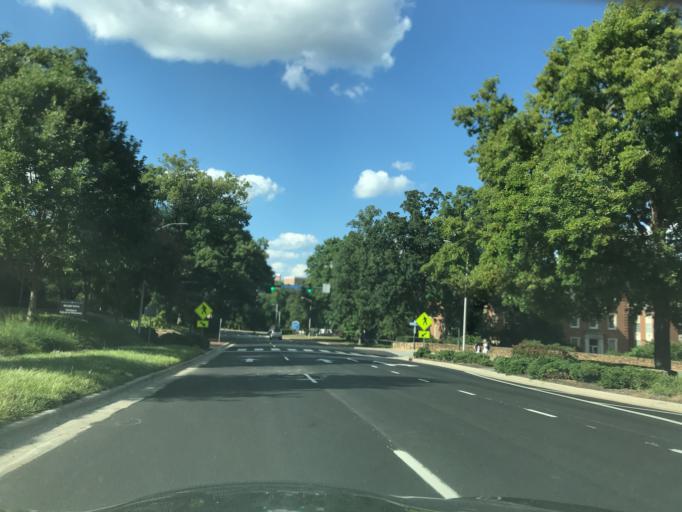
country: US
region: North Carolina
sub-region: Orange County
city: Chapel Hill
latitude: 35.9067
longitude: -79.0530
